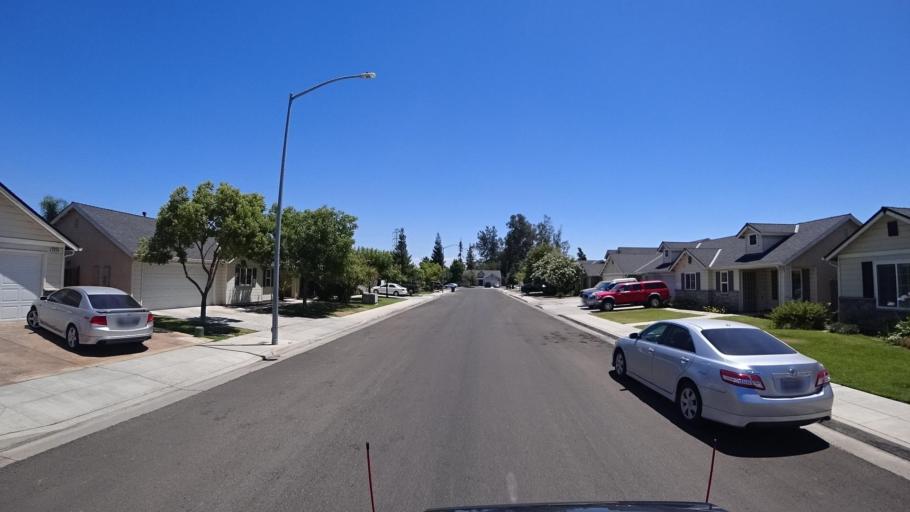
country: US
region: California
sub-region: Fresno County
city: Sunnyside
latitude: 36.7357
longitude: -119.6703
